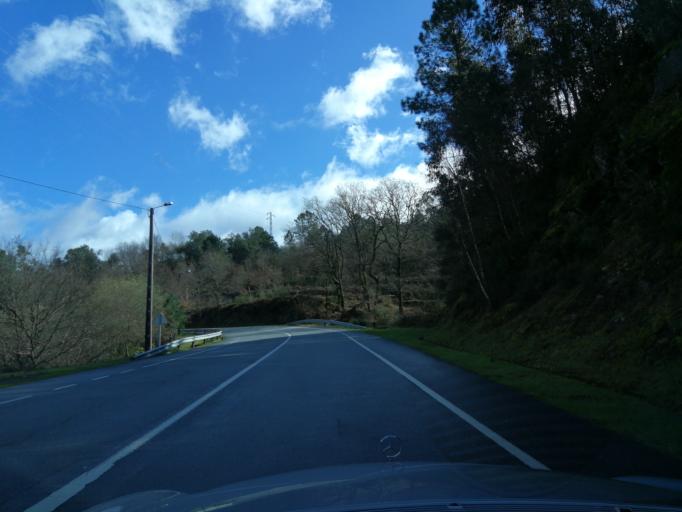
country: ES
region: Galicia
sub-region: Provincia de Ourense
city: Entrimo
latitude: 41.8652
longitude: -8.2123
